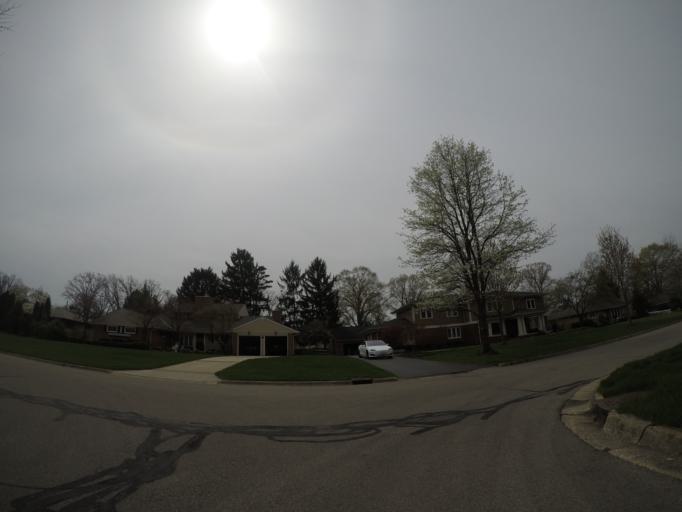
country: US
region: Ohio
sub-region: Franklin County
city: Upper Arlington
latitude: 40.0158
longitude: -83.0806
